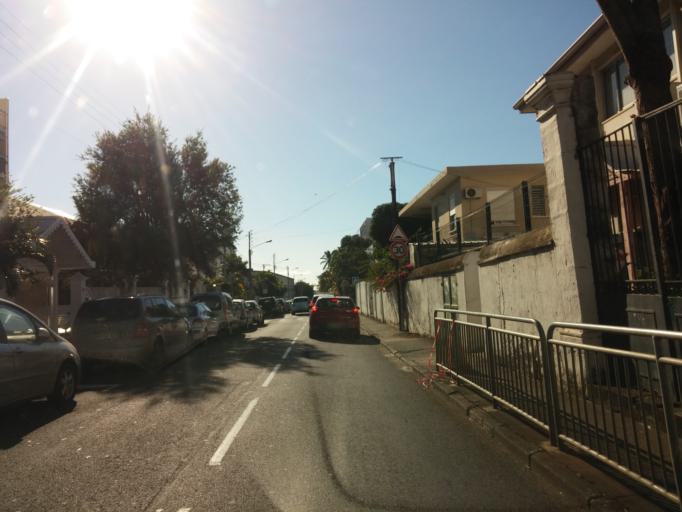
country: RE
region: Reunion
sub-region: Reunion
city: Saint-Denis
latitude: -20.8836
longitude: 55.4481
